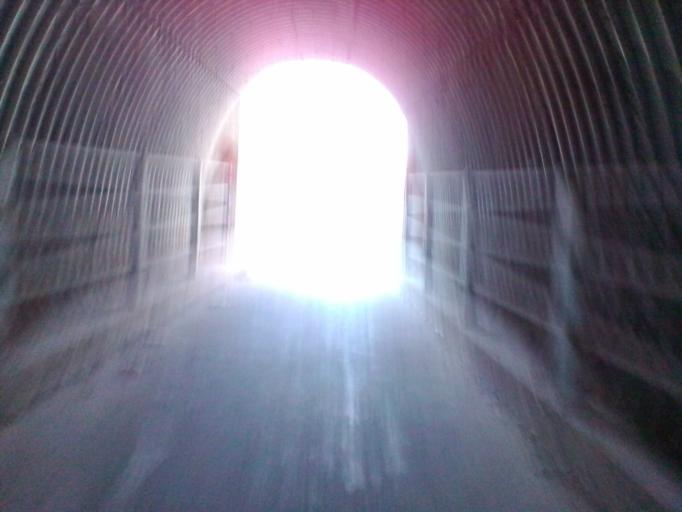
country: IT
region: Lombardy
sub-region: Provincia di Mantova
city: Marmirolo
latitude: 45.2276
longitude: 10.7264
